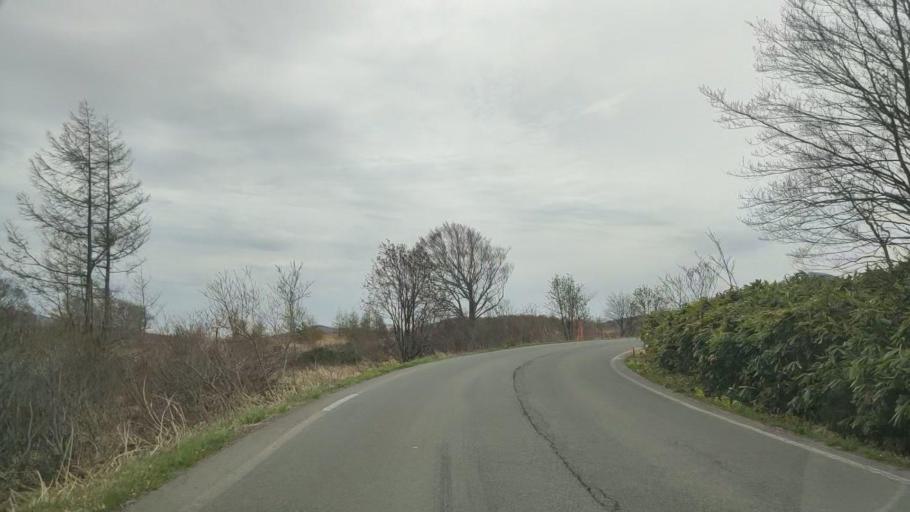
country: JP
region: Aomori
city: Aomori Shi
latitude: 40.6882
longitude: 140.9241
